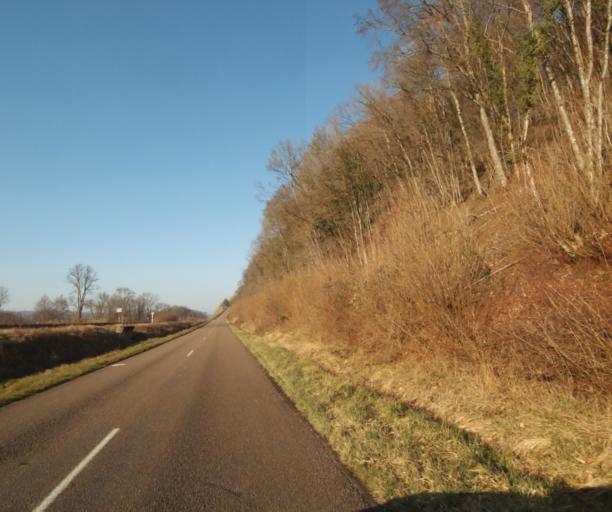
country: FR
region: Champagne-Ardenne
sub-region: Departement de la Haute-Marne
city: Chevillon
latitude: 48.5117
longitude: 5.1210
